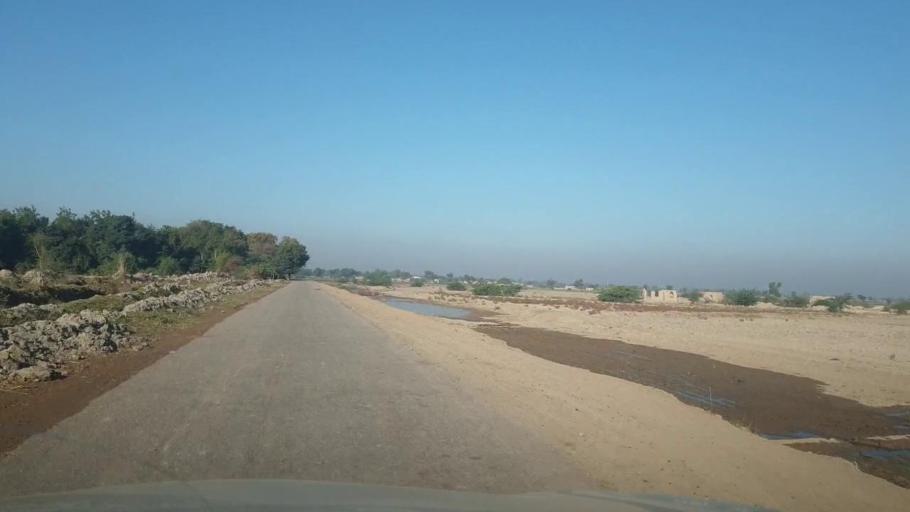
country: PK
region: Sindh
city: Bhan
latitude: 26.5528
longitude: 67.6949
